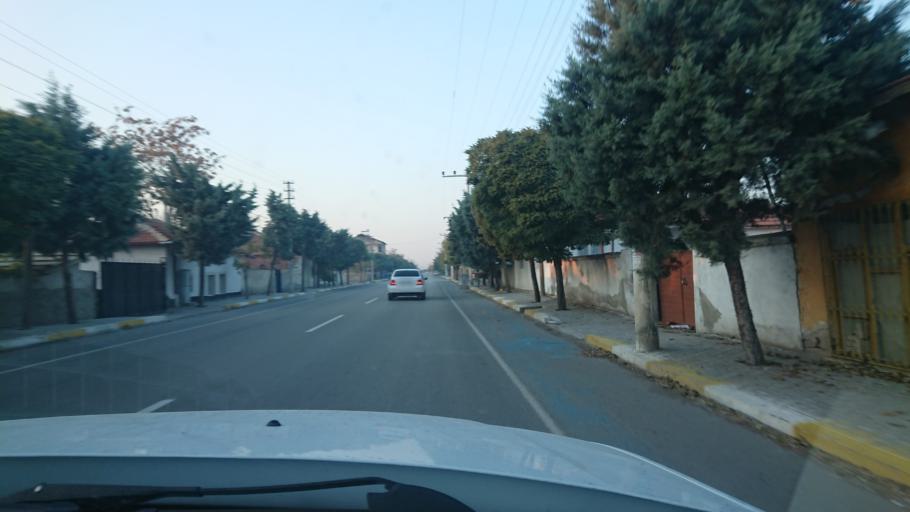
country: TR
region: Aksaray
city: Aksaray
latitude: 38.3036
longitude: 34.0694
